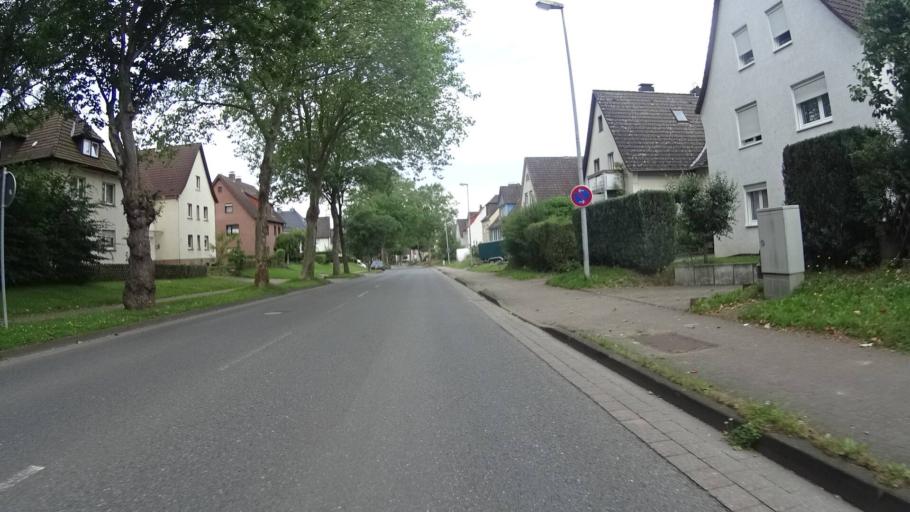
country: DE
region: Lower Saxony
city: Holzminden
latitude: 51.8273
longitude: 9.4775
